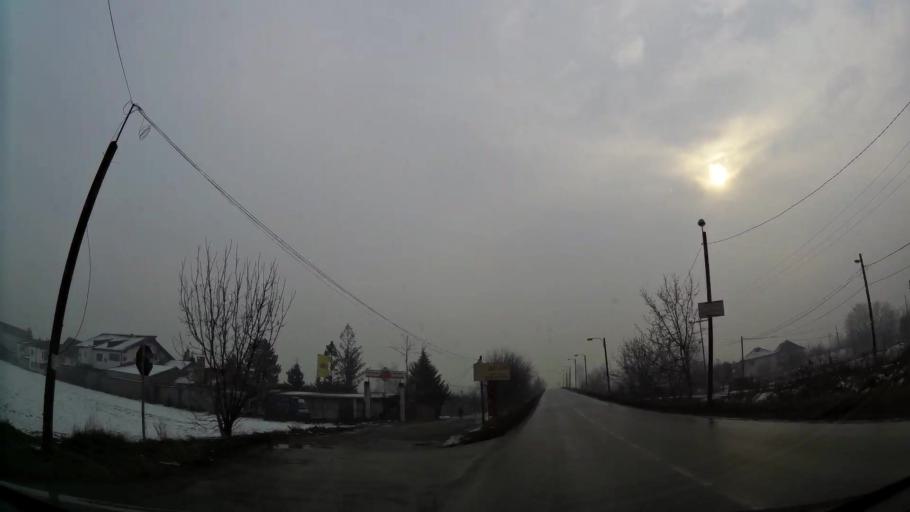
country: MK
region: Ilinden
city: Jurumleri
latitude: 41.9716
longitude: 21.5425
